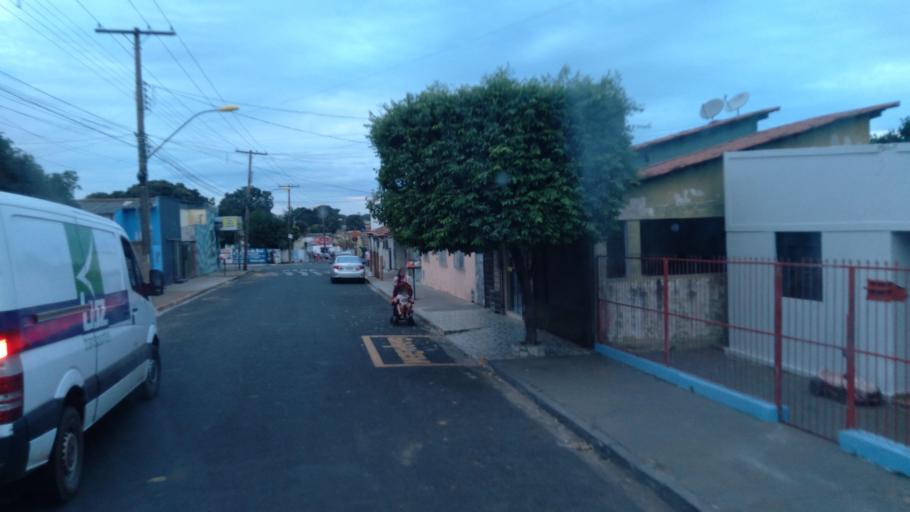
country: BR
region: Goias
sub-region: Mineiros
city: Mineiros
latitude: -17.5657
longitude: -52.5481
